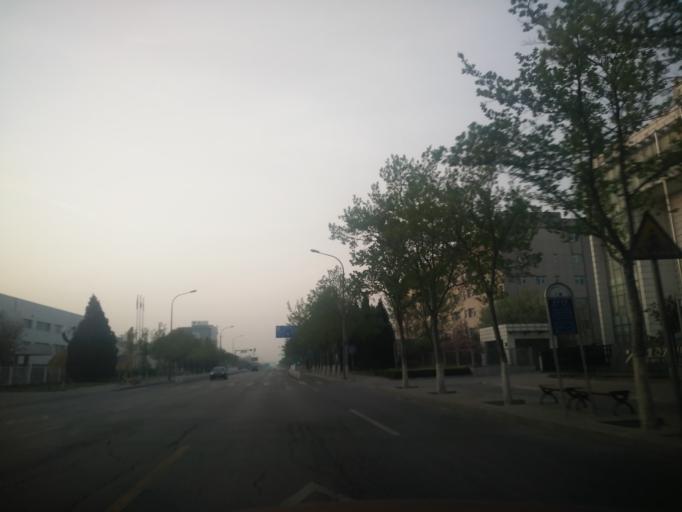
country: CN
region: Beijing
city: Jiugong
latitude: 39.7966
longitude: 116.5095
